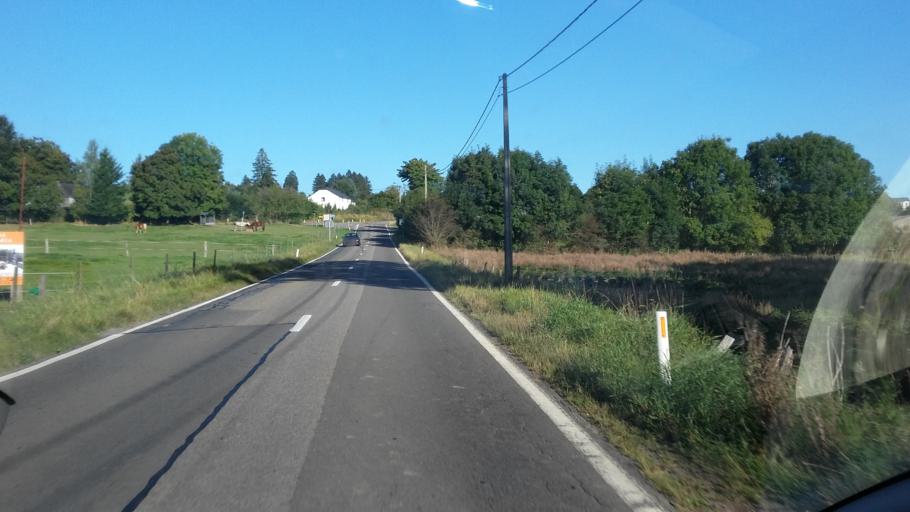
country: BE
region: Wallonia
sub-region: Province du Luxembourg
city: Neufchateau
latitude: 49.8303
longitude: 5.4813
